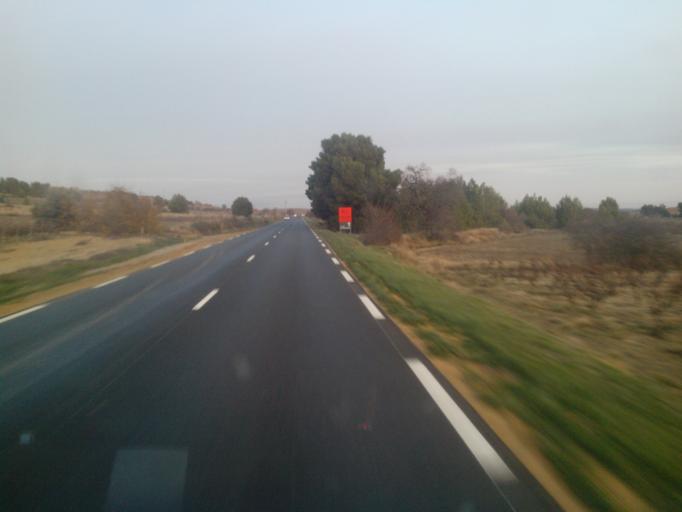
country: FR
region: Languedoc-Roussillon
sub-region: Departement de l'Aude
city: Ginestas
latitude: 43.2873
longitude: 2.8530
